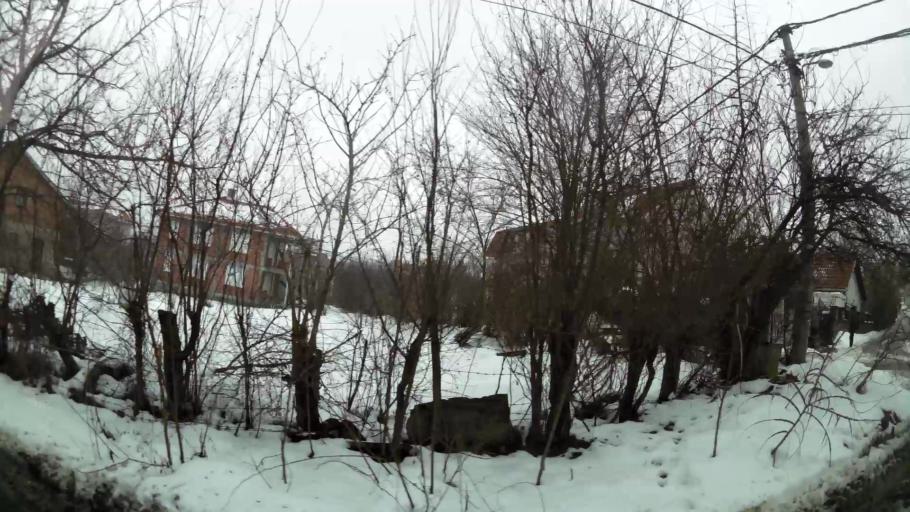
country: RS
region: Central Serbia
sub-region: Belgrade
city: Zvezdara
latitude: 44.7457
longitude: 20.5153
